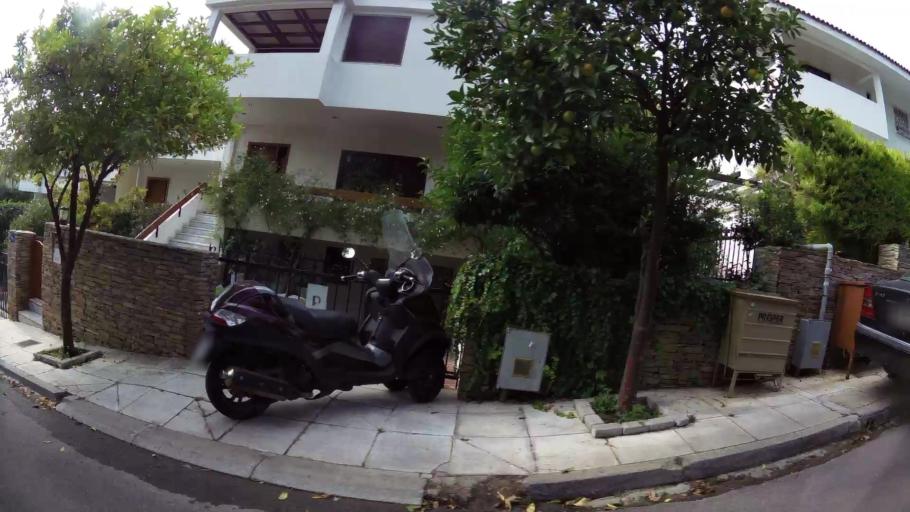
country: GR
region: Attica
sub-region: Nomarchia Athinas
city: Psychiko
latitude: 38.0182
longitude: 23.7659
